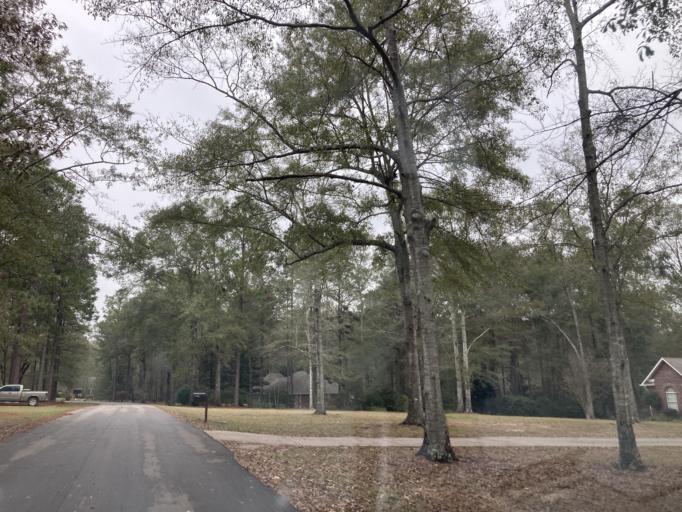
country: US
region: Mississippi
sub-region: Lamar County
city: Purvis
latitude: 31.1545
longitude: -89.4221
